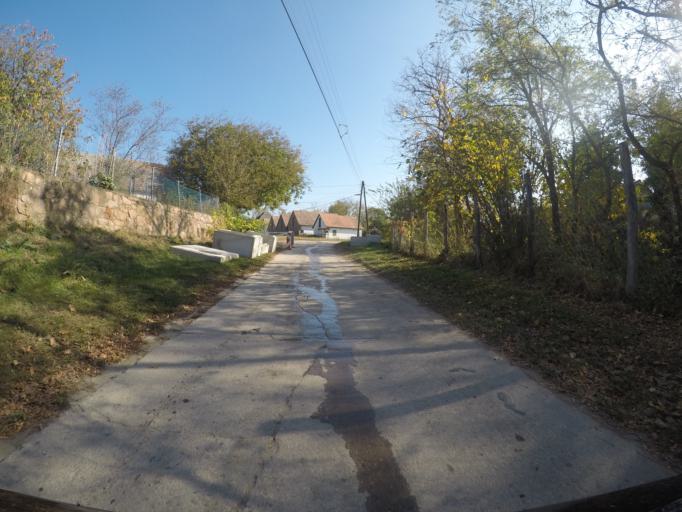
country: HU
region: Tolna
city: Nagydorog
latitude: 46.6366
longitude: 18.7021
